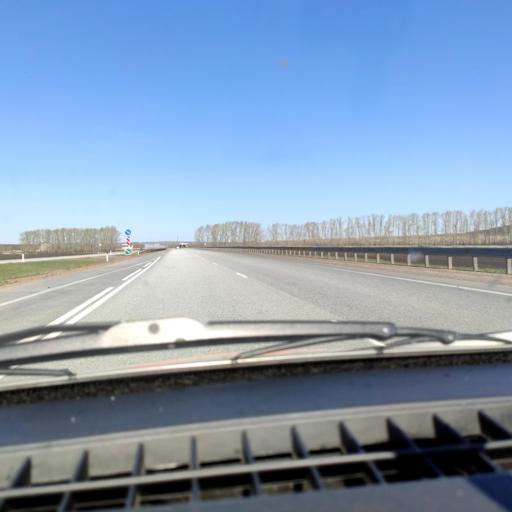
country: RU
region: Bashkortostan
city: Asanovo
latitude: 54.9549
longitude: 55.5852
